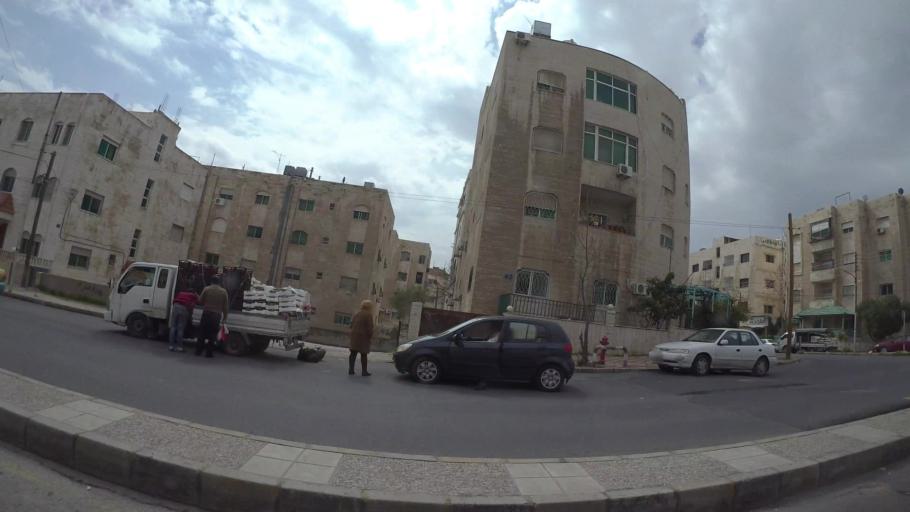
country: JO
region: Amman
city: Amman
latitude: 31.9878
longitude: 35.9227
